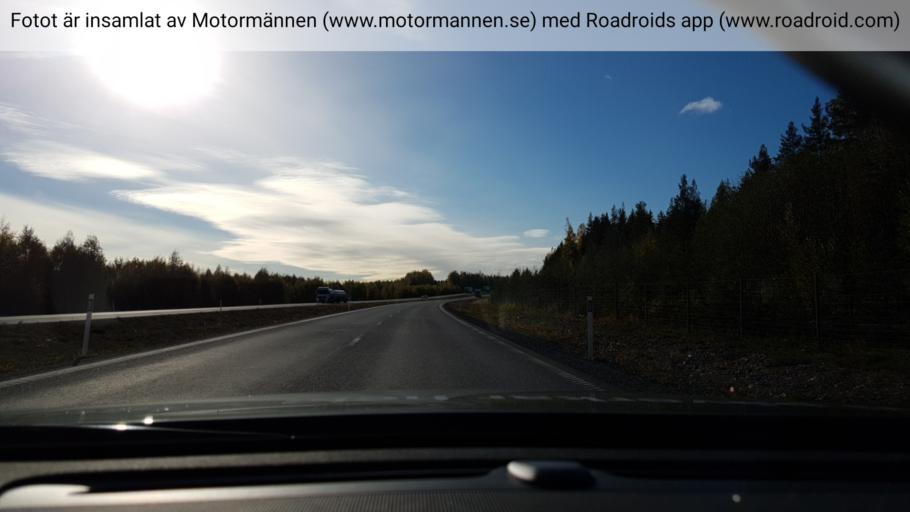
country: SE
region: Vaesterbotten
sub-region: Skelleftea Kommun
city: Kage
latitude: 64.8134
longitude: 21.0301
